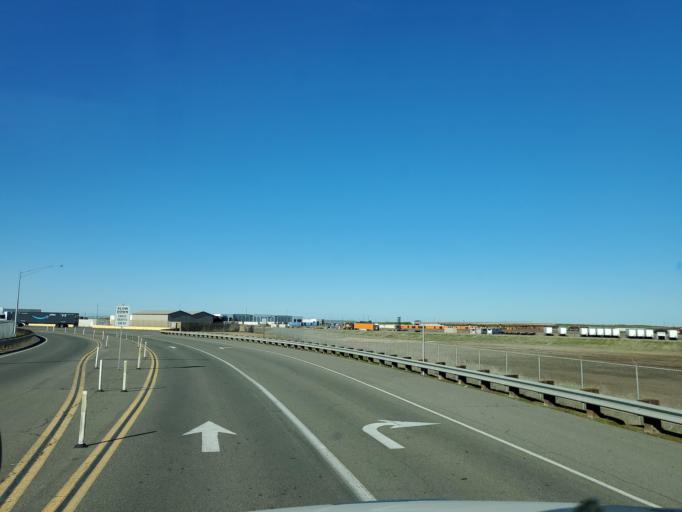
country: US
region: California
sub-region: San Joaquin County
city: Garden Acres
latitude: 37.9049
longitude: -121.1789
